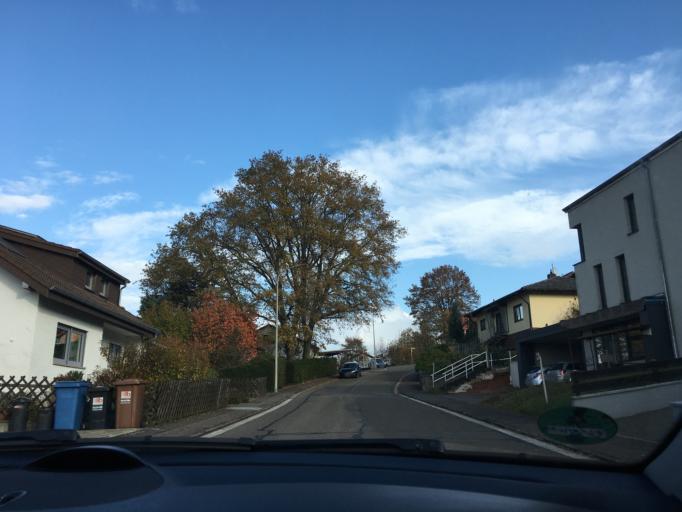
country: DE
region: Rheinland-Pfalz
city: Schopp
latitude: 49.3456
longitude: 7.6842
